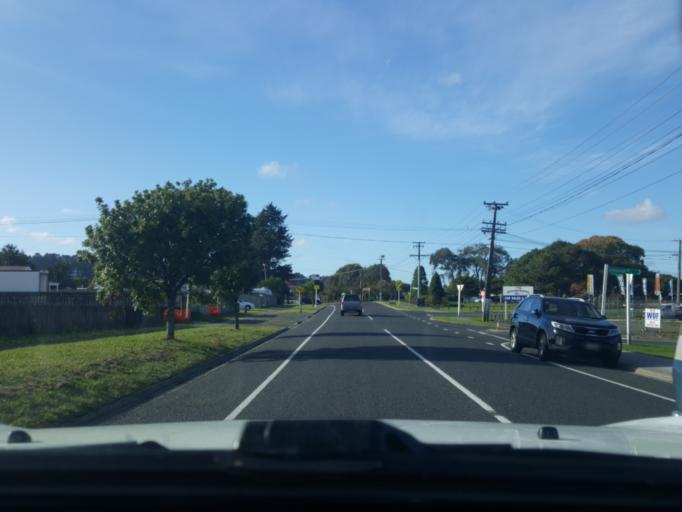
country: NZ
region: Auckland
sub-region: Auckland
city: Rosebank
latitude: -36.7591
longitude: 174.5908
